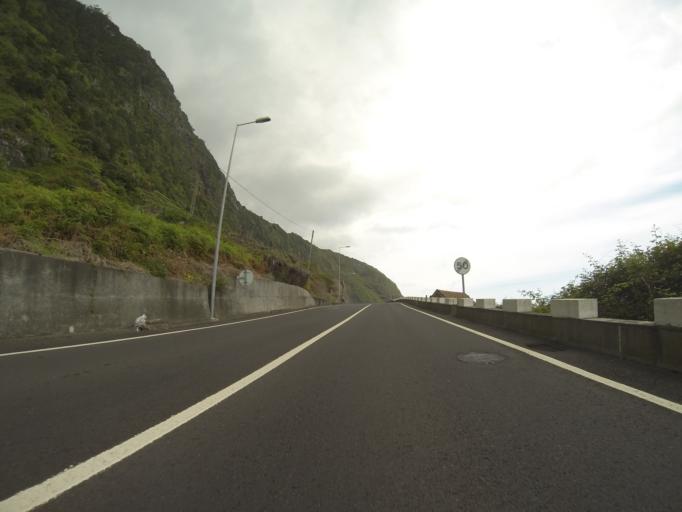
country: PT
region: Madeira
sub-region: Porto Moniz
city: Porto Moniz
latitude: 32.8460
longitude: -17.1473
